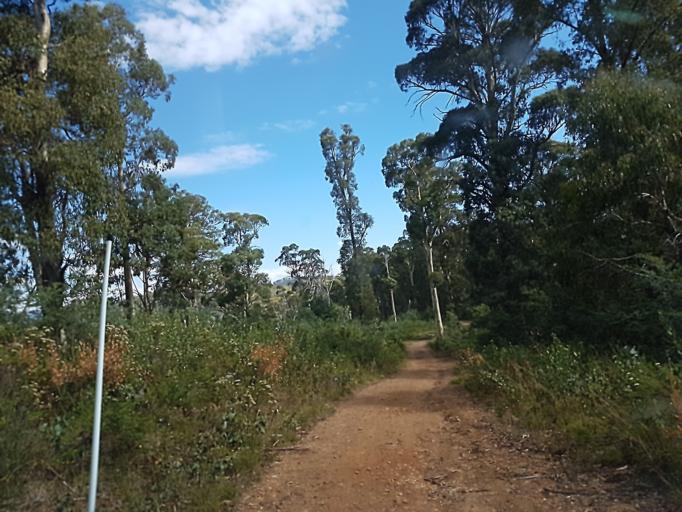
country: AU
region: Victoria
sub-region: Alpine
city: Mount Beauty
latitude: -36.9200
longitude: 146.9972
